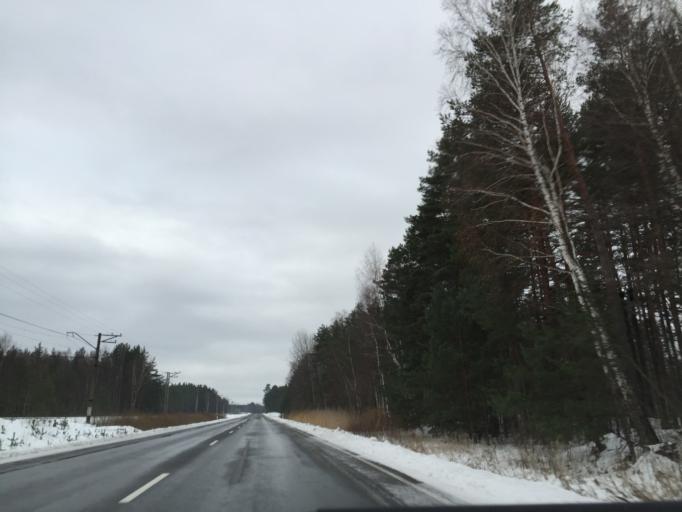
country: LV
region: Saulkrastu
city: Saulkrasti
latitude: 57.2058
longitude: 24.3771
